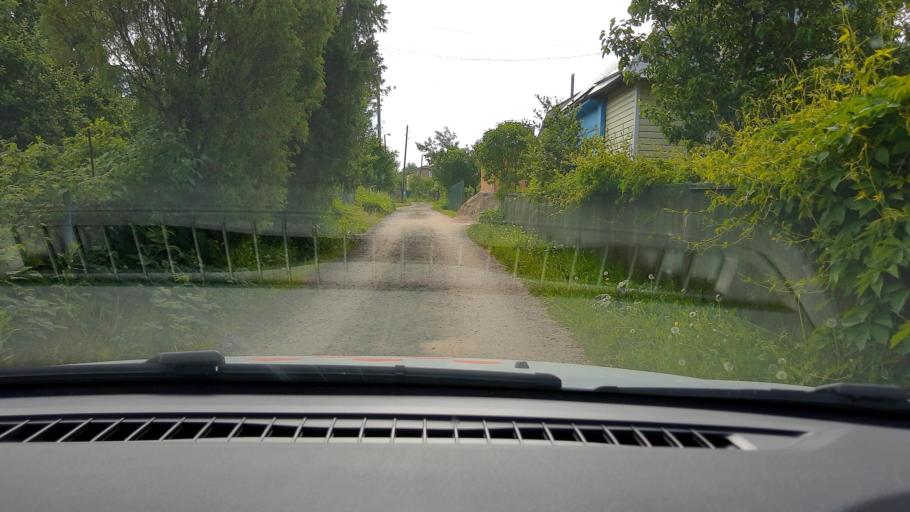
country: RU
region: Nizjnij Novgorod
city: Linda
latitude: 56.6610
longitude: 44.1732
